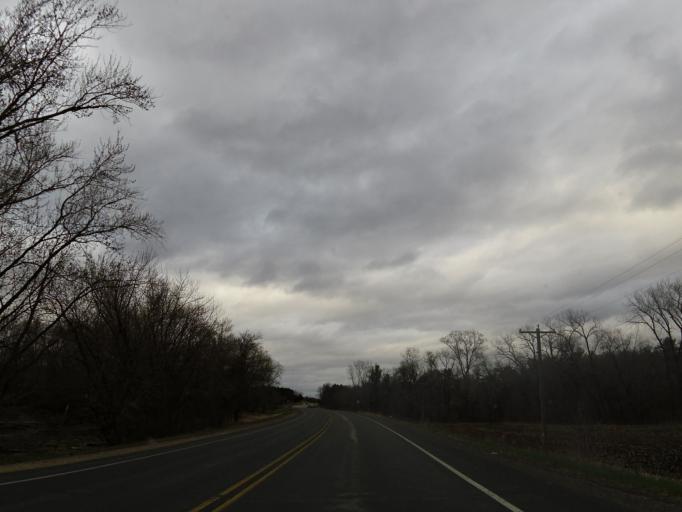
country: US
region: Wisconsin
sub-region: Saint Croix County
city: Roberts
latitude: 45.0441
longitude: -92.6250
